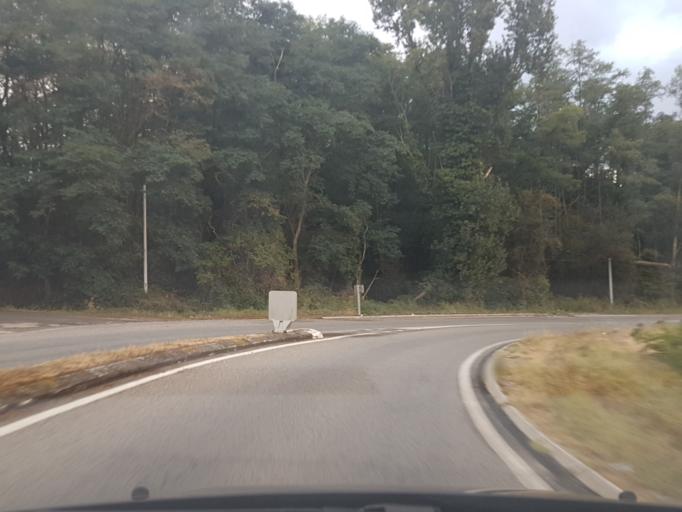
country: FR
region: Midi-Pyrenees
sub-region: Departement de l'Ariege
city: La Tour-du-Crieu
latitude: 43.0922
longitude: 1.6814
